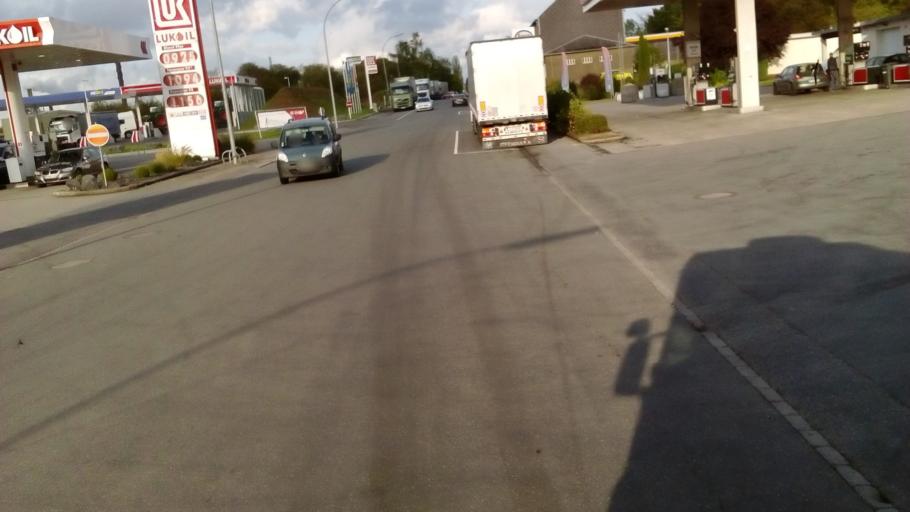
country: FR
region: Lorraine
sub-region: Departement de Meurthe-et-Moselle
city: Saulnes
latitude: 49.5423
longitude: 5.8169
